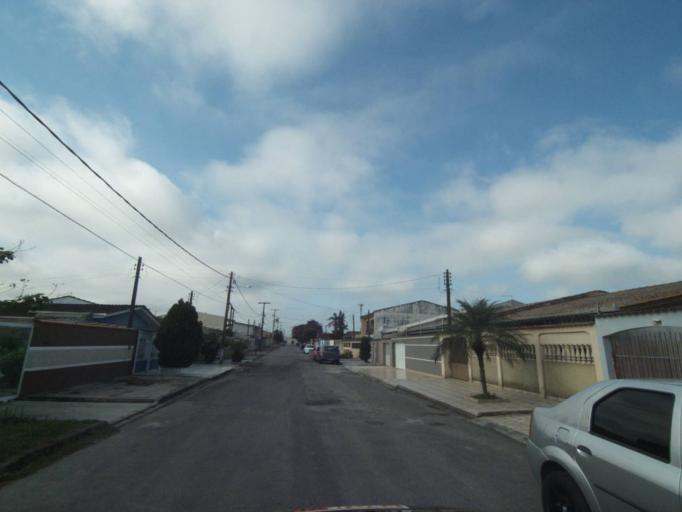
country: BR
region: Parana
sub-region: Paranagua
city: Paranagua
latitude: -25.5565
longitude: -48.5601
